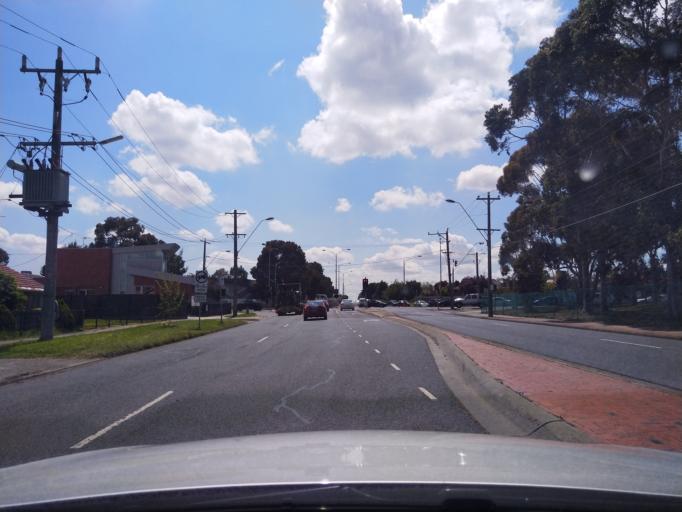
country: AU
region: Victoria
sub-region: Banyule
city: Bellfield
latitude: -37.7520
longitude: 145.0459
